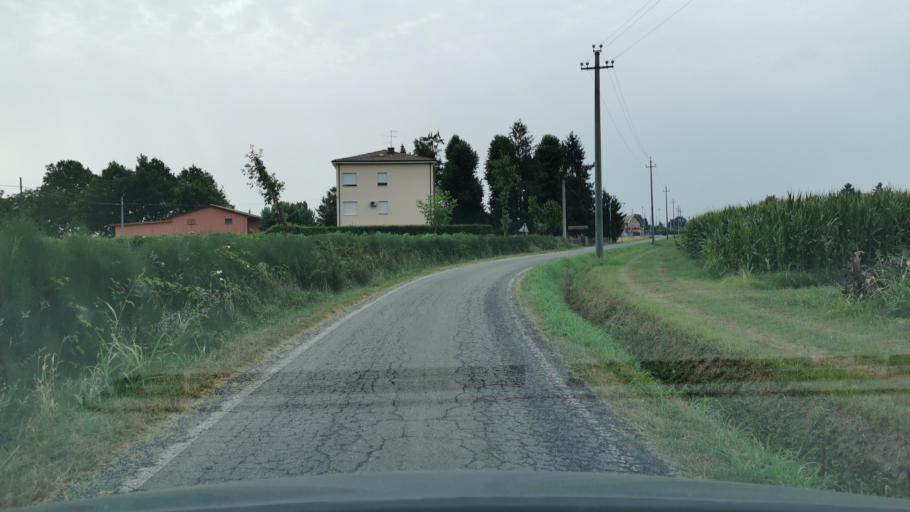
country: IT
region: Emilia-Romagna
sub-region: Provincia di Modena
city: Campogalliano
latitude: 44.6857
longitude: 10.8792
